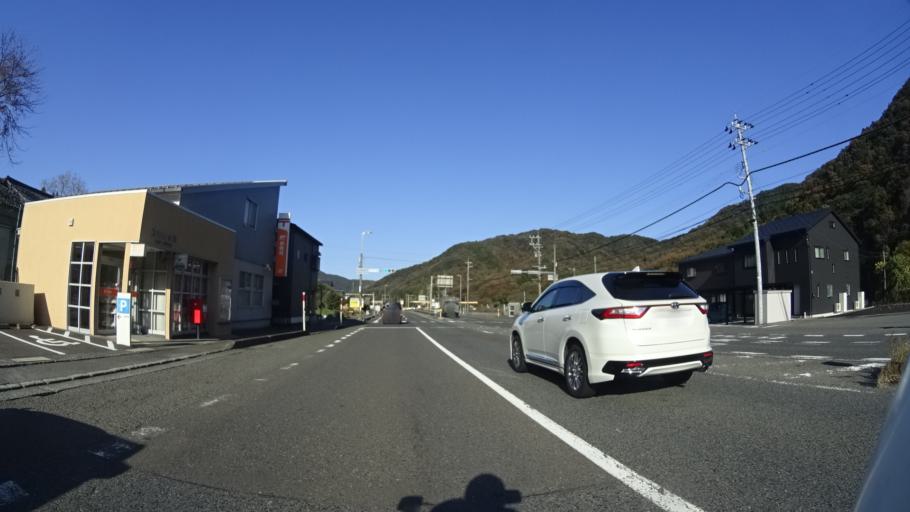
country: JP
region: Fukui
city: Tsuruga
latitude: 35.6029
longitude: 136.0994
